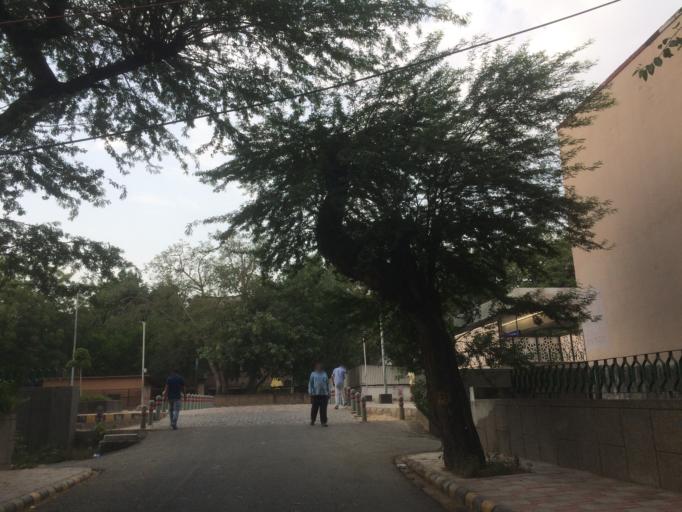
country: IN
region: NCT
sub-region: New Delhi
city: New Delhi
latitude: 28.5762
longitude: 77.1999
